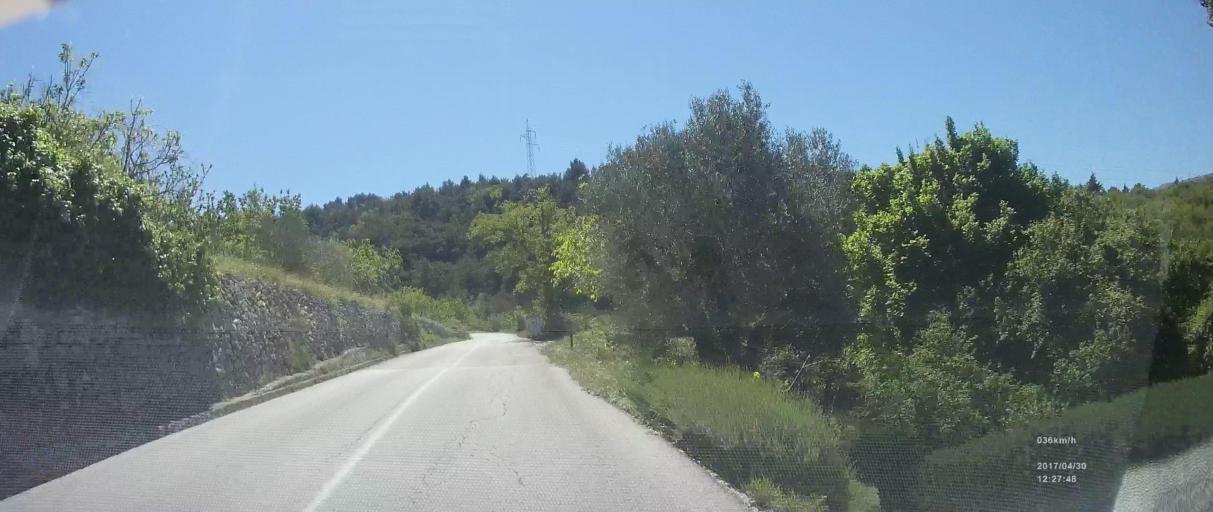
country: HR
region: Splitsko-Dalmatinska
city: Srinjine
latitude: 43.5055
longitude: 16.5987
